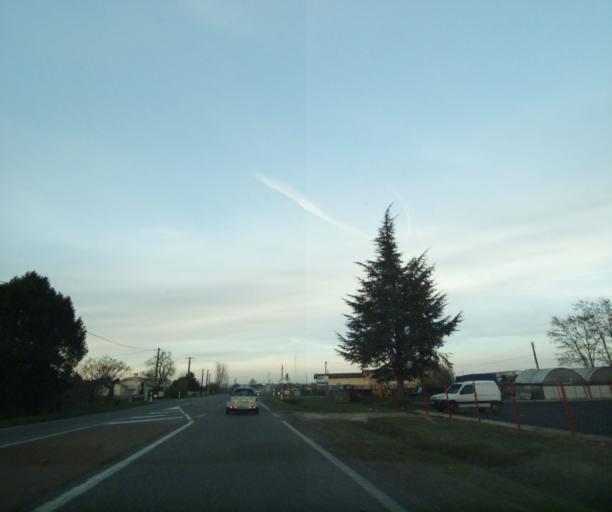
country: FR
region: Aquitaine
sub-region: Departement de la Gironde
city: Langon
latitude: 44.5277
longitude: -0.2407
